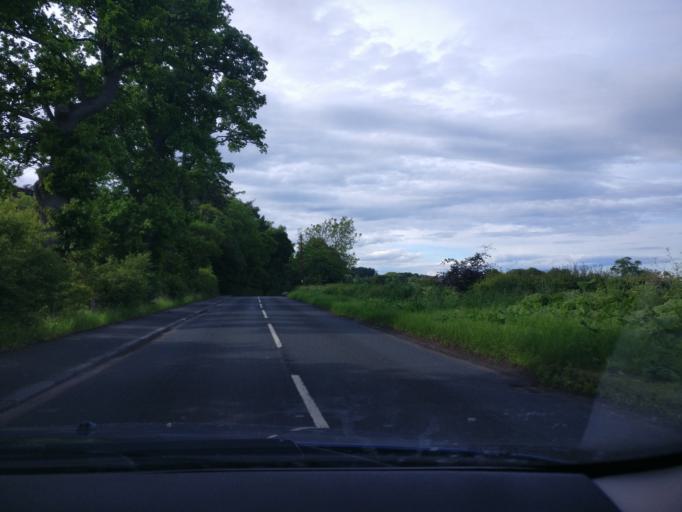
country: GB
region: Scotland
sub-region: East Lothian
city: Haddington
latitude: 55.9056
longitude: -2.7464
